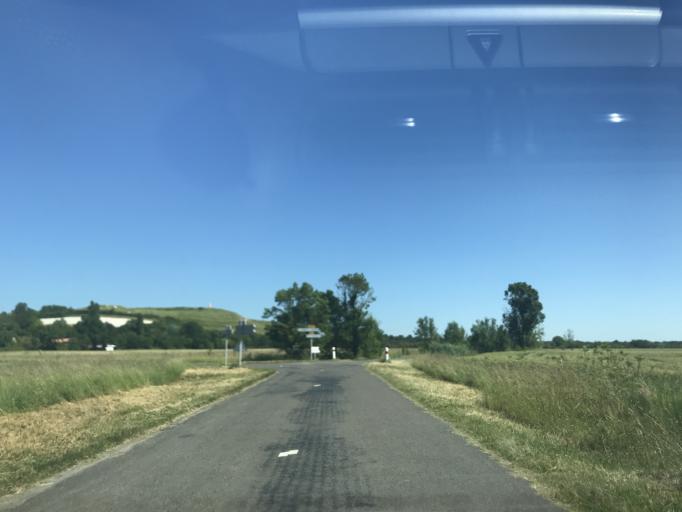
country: FR
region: Poitou-Charentes
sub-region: Departement de la Charente-Maritime
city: Mortagne-sur-Gironde
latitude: 45.4492
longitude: -0.7625
